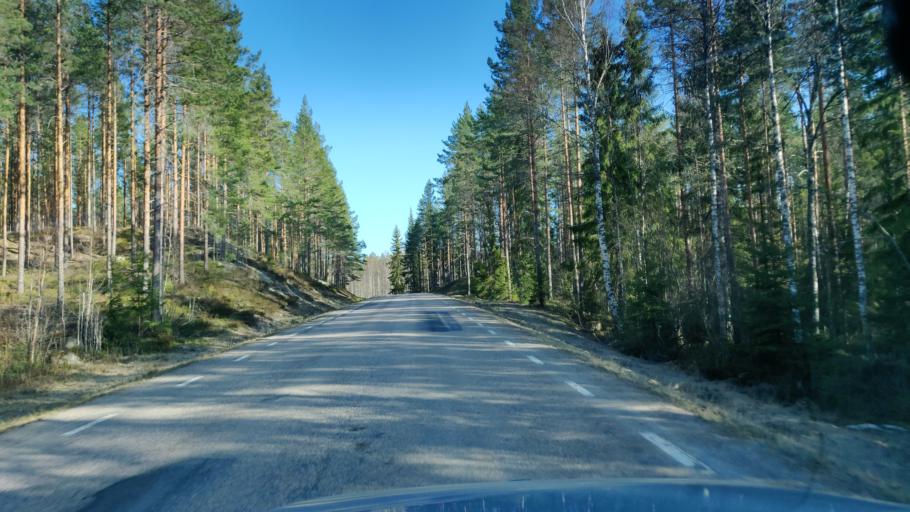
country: SE
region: Vaermland
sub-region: Sunne Kommun
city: Sunne
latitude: 59.9877
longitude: 13.3142
